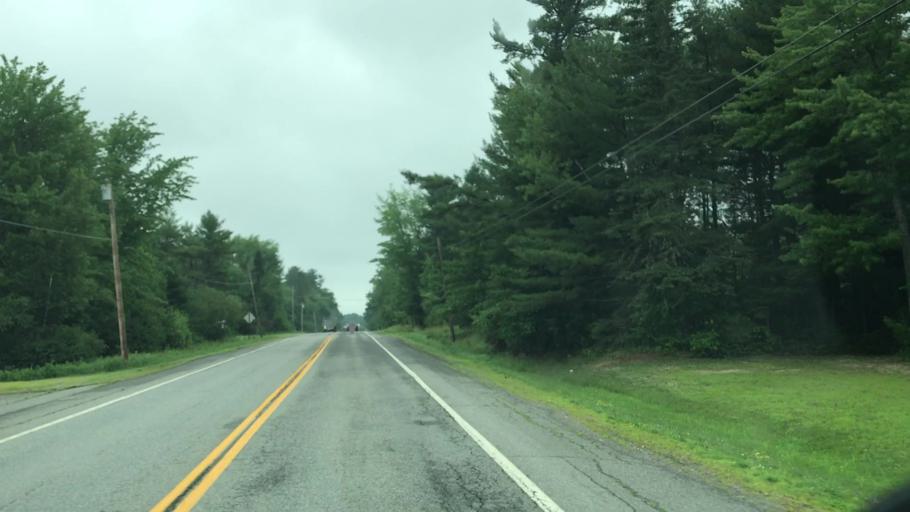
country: US
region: Maine
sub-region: Penobscot County
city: Howland
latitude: 45.2890
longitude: -68.6236
